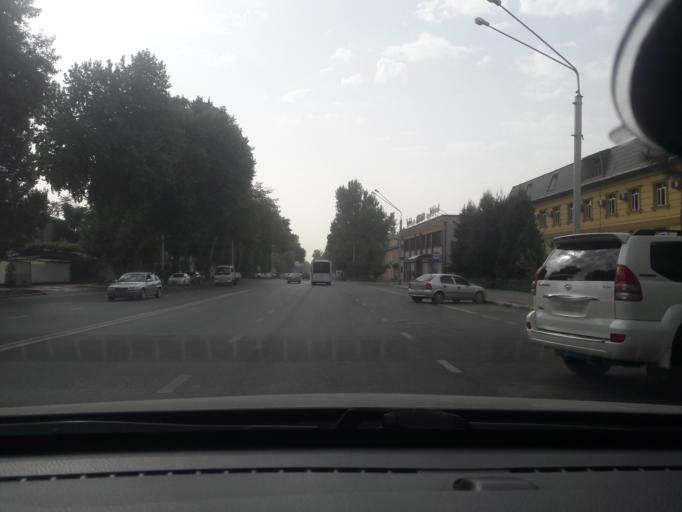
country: TJ
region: Dushanbe
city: Dushanbe
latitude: 38.5777
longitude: 68.8023
